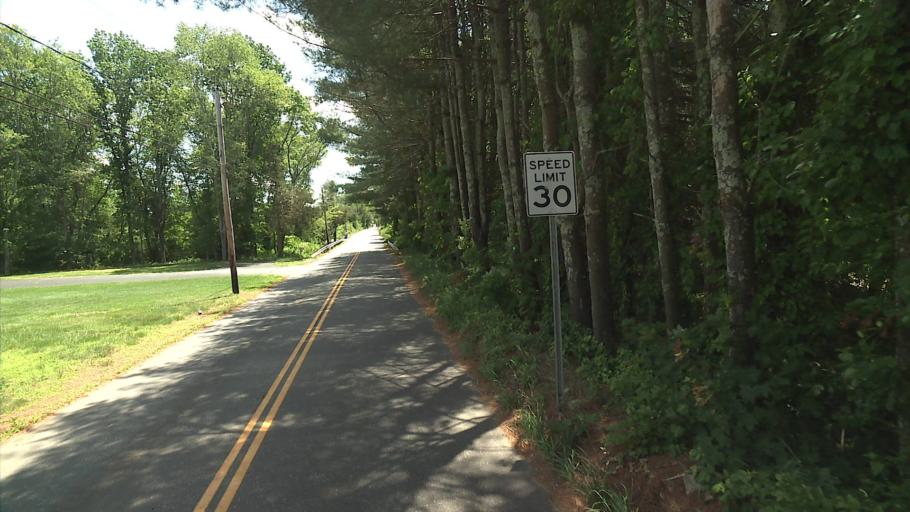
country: US
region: Connecticut
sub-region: New London County
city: Jewett City
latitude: 41.6122
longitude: -71.9337
